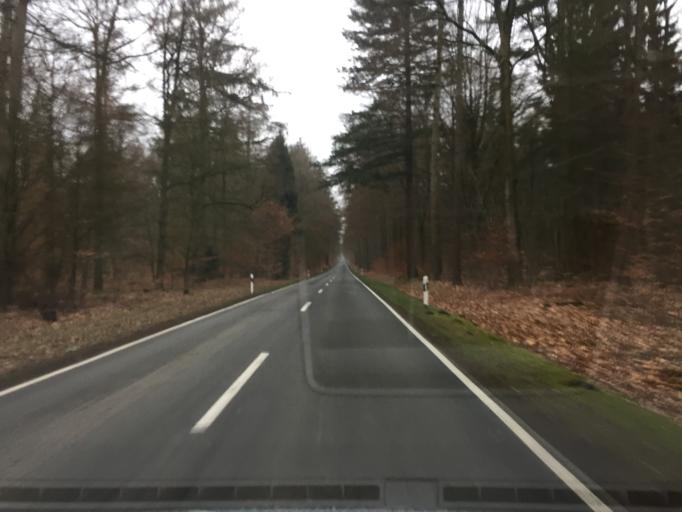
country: DE
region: Lower Saxony
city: Sudwalde
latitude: 52.8235
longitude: 8.8414
